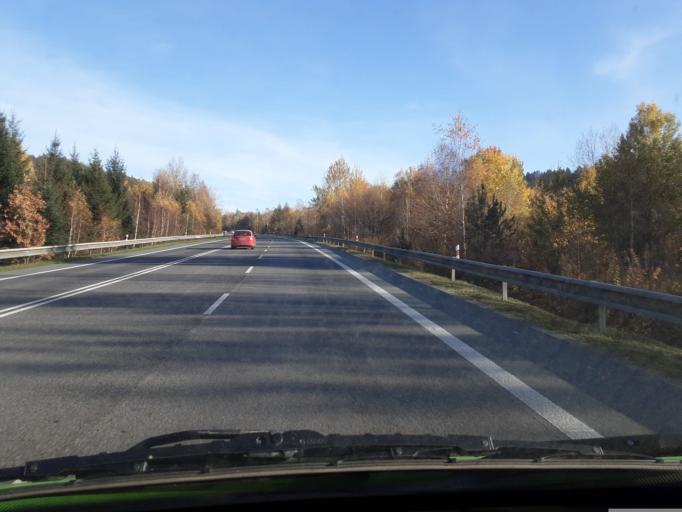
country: CZ
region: Plzensky
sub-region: Okres Klatovy
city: Kolinec
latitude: 49.3547
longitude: 13.4043
